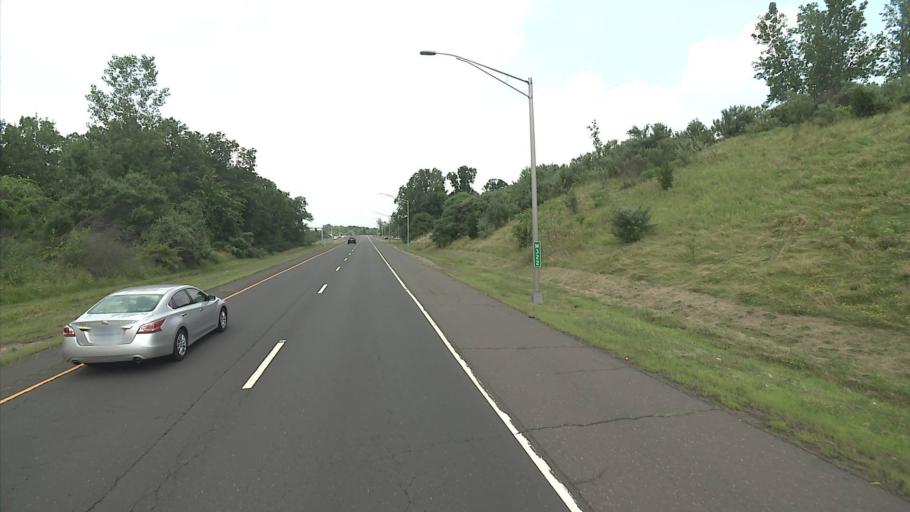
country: US
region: Connecticut
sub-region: Hartford County
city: East Hartford
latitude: 41.7898
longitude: -72.5679
